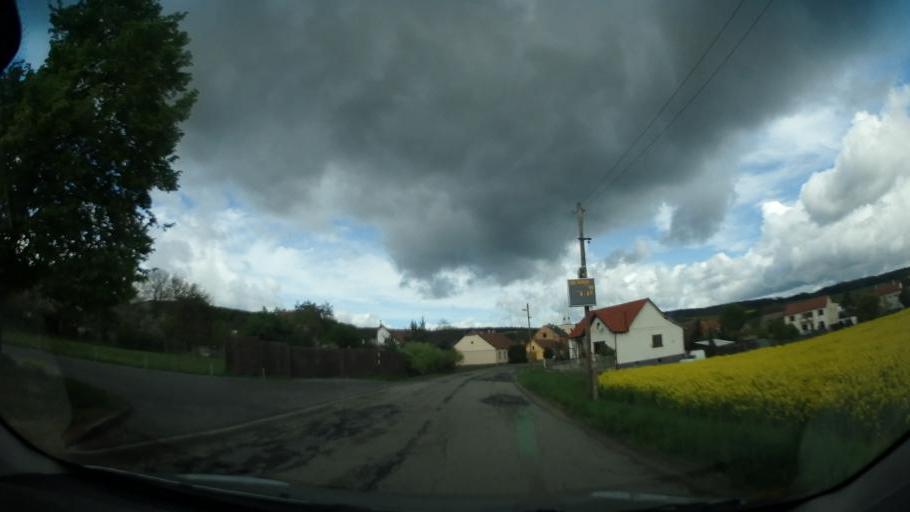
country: CZ
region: South Moravian
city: Ricany
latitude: 49.2333
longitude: 16.4068
